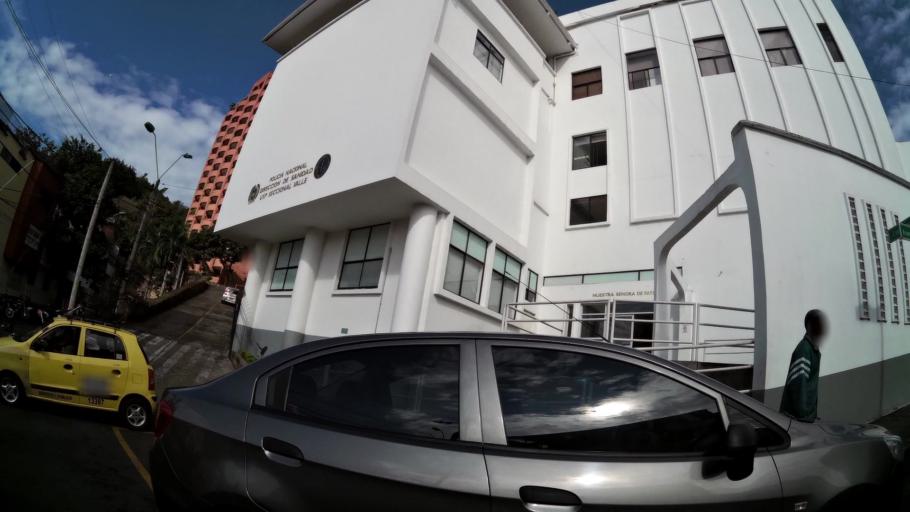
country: CO
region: Valle del Cauca
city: Cali
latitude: 3.4616
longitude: -76.5345
